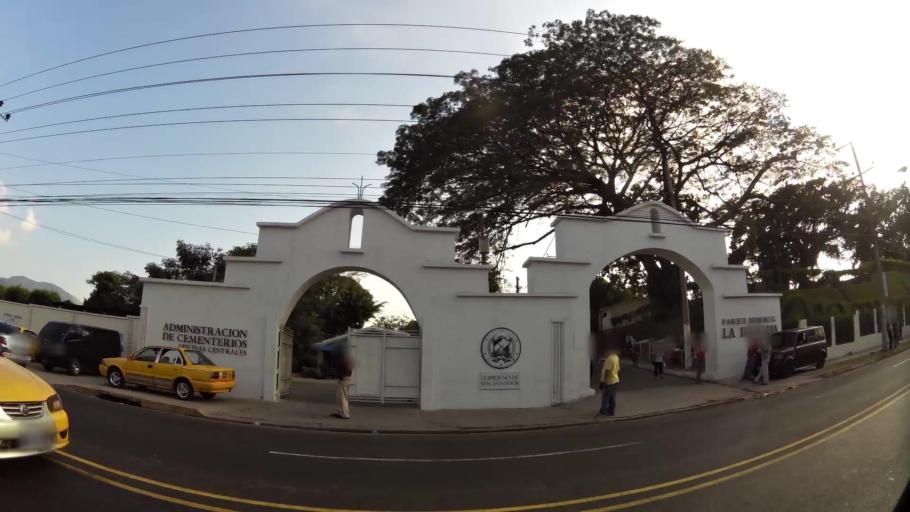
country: SV
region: San Salvador
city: San Salvador
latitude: 13.6920
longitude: -89.2082
